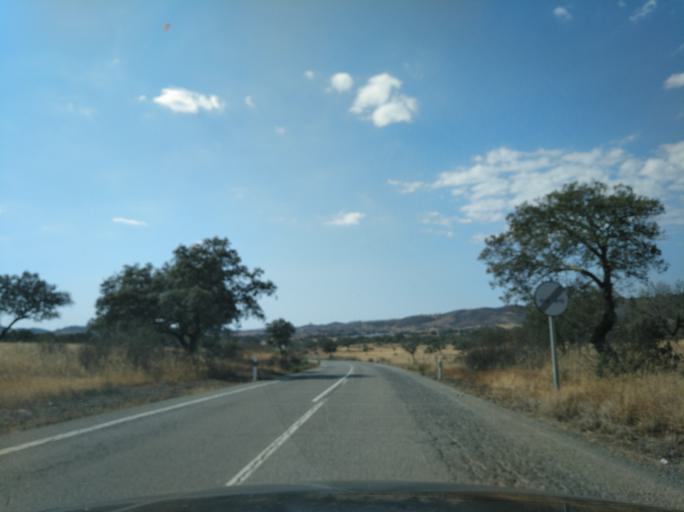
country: ES
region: Andalusia
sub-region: Provincia de Huelva
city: Santa Barbara de Casa
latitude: 37.7735
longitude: -7.1469
